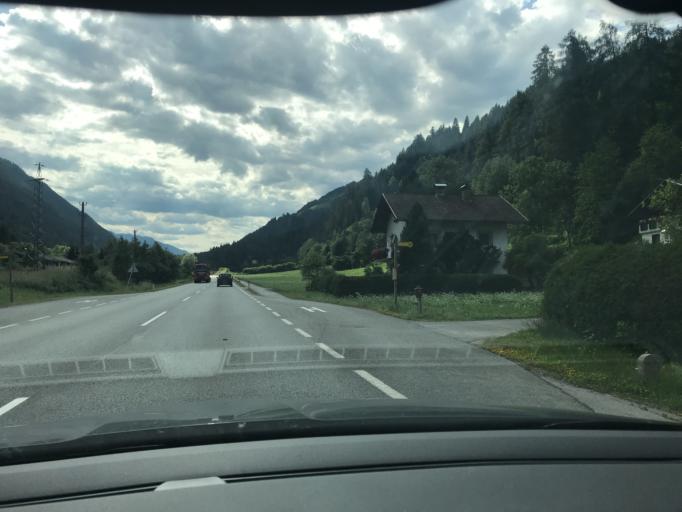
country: AT
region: Tyrol
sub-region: Politischer Bezirk Lienz
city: Obertilliach
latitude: 46.7812
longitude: 12.6474
